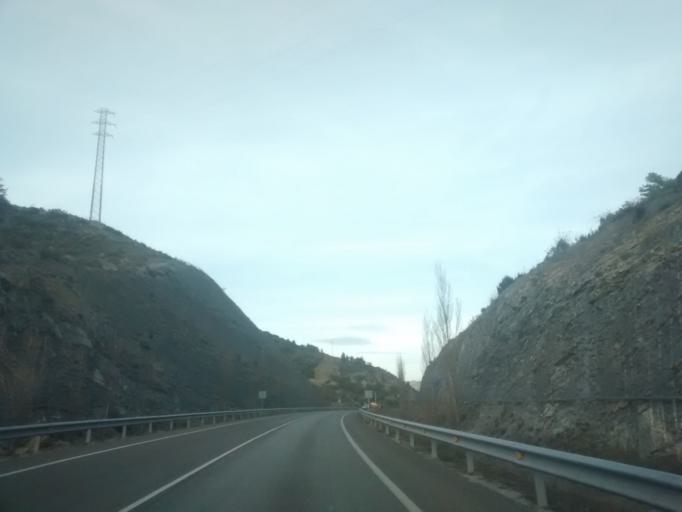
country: ES
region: Catalonia
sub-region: Provincia de Lleida
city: Coll de Nargo
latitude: 42.1510
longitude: 1.3075
